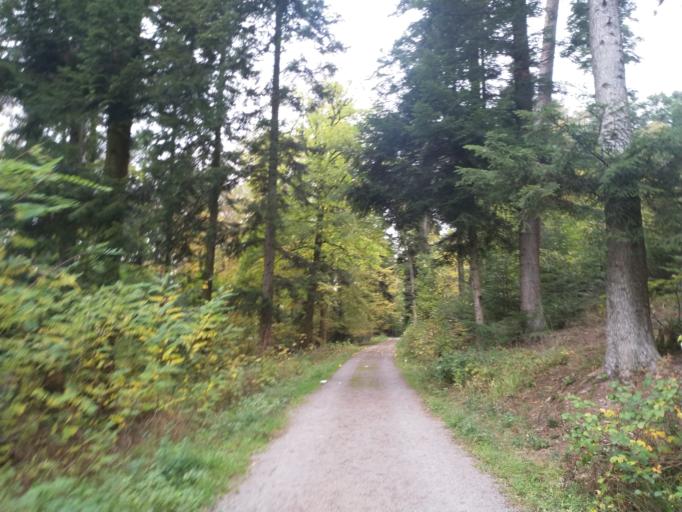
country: DE
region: Baden-Wuerttemberg
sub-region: Karlsruhe Region
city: Birkenfeld
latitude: 48.8577
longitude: 8.6463
